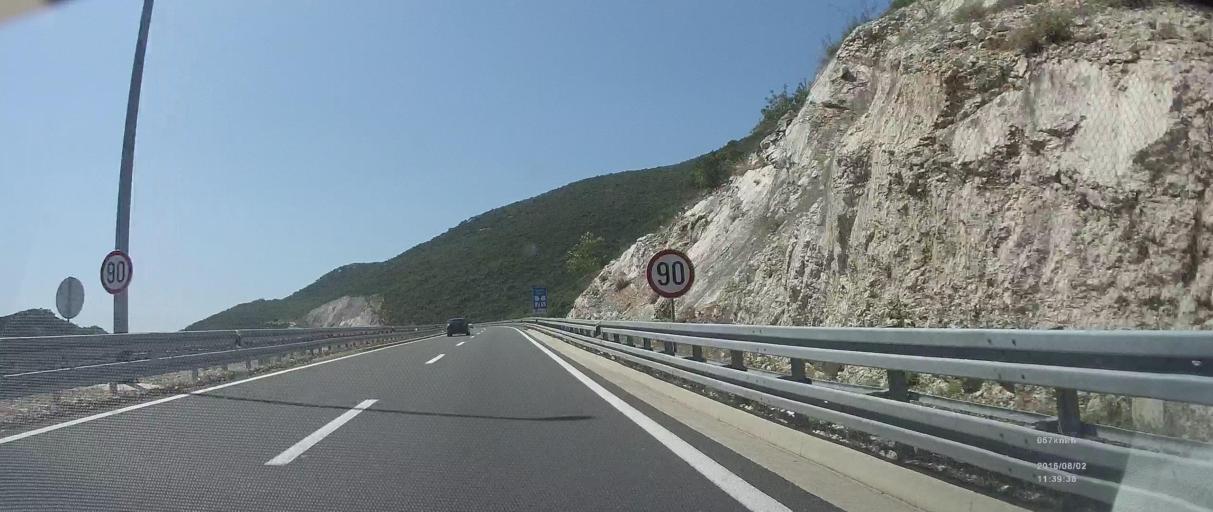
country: HR
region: Dubrovacko-Neretvanska
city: Komin
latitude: 43.0838
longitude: 17.4907
